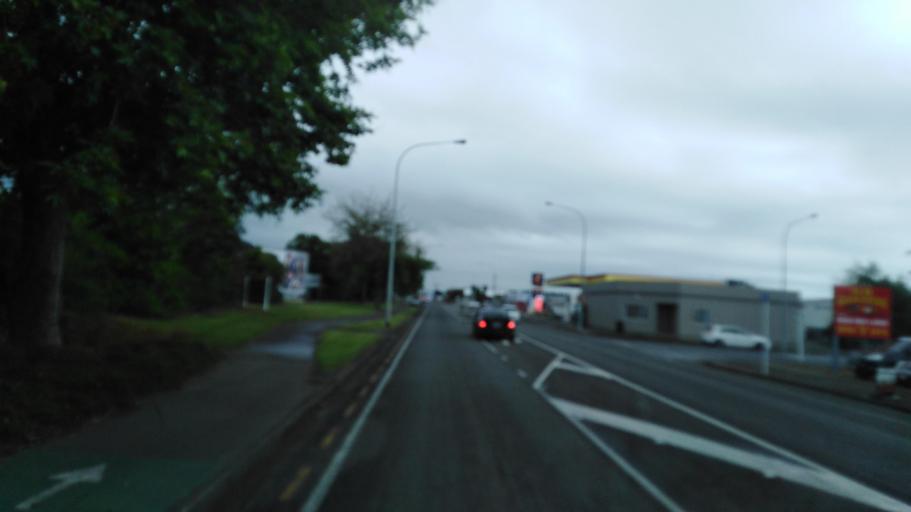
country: NZ
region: Manawatu-Wanganui
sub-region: Horowhenua District
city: Levin
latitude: -40.6315
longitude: 175.2772
